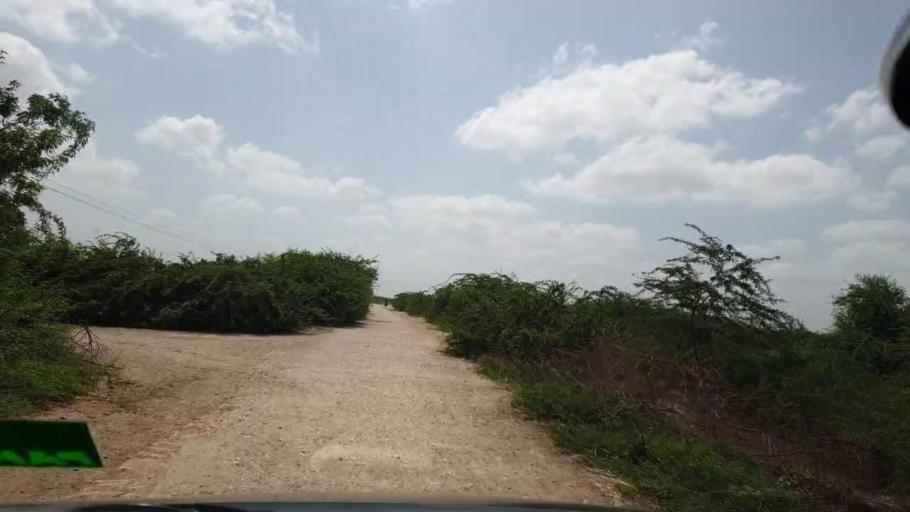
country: PK
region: Sindh
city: Kadhan
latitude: 24.5549
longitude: 69.2113
